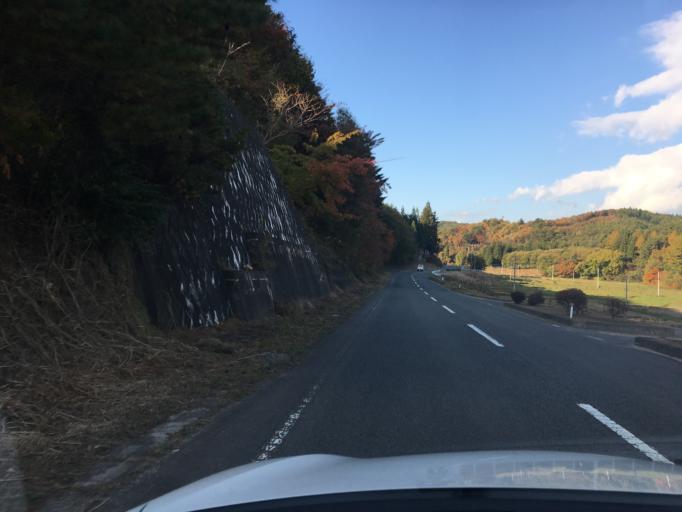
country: JP
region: Fukushima
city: Iwaki
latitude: 37.2649
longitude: 140.7646
